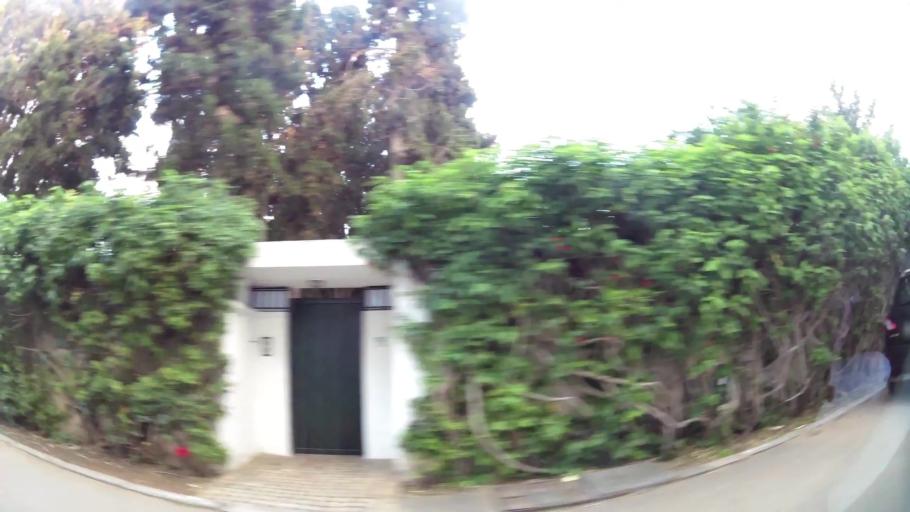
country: MA
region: Rabat-Sale-Zemmour-Zaer
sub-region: Rabat
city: Rabat
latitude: 33.9718
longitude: -6.8403
